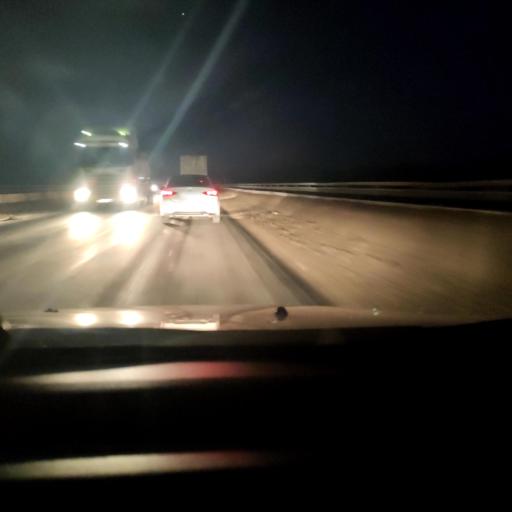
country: RU
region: Samara
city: Smyshlyayevka
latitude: 53.2351
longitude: 50.4868
